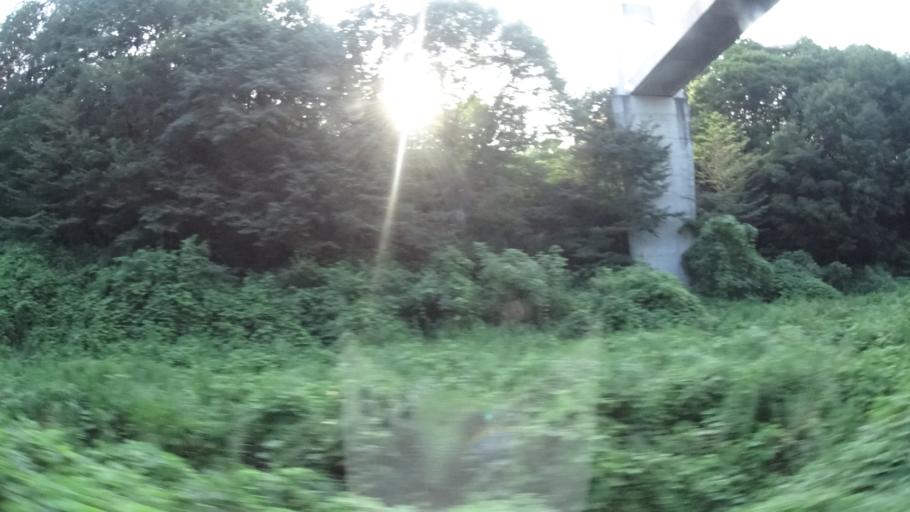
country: JP
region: Tochigi
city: Karasuyama
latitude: 36.6103
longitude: 140.1538
